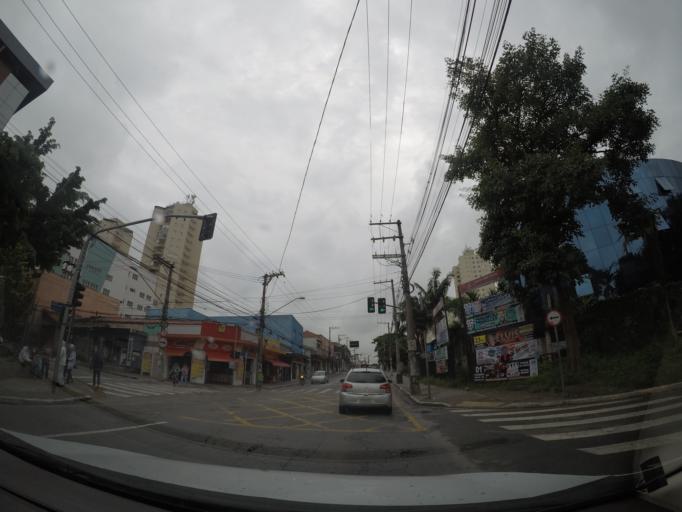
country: BR
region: Sao Paulo
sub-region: Guarulhos
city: Guarulhos
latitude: -23.4694
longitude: -46.5197
